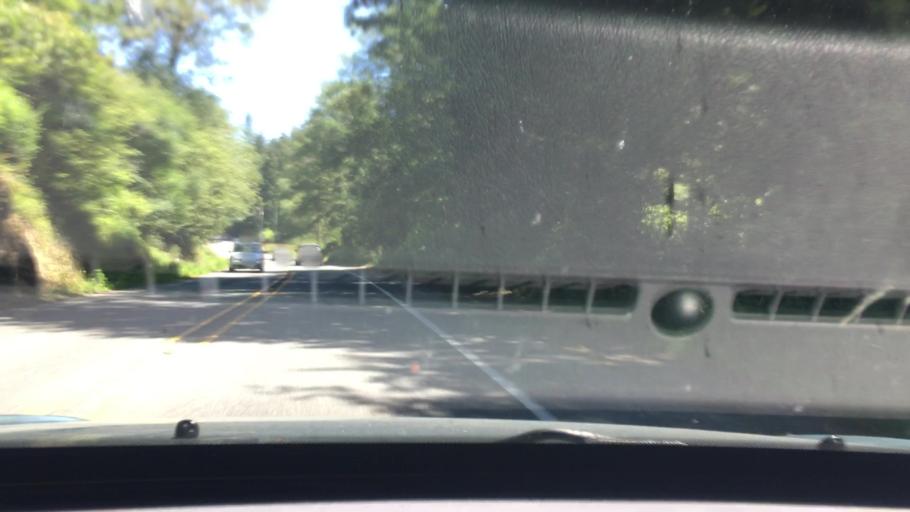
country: US
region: Washington
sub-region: King County
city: East Renton Highlands
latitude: 47.5110
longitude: -122.0839
